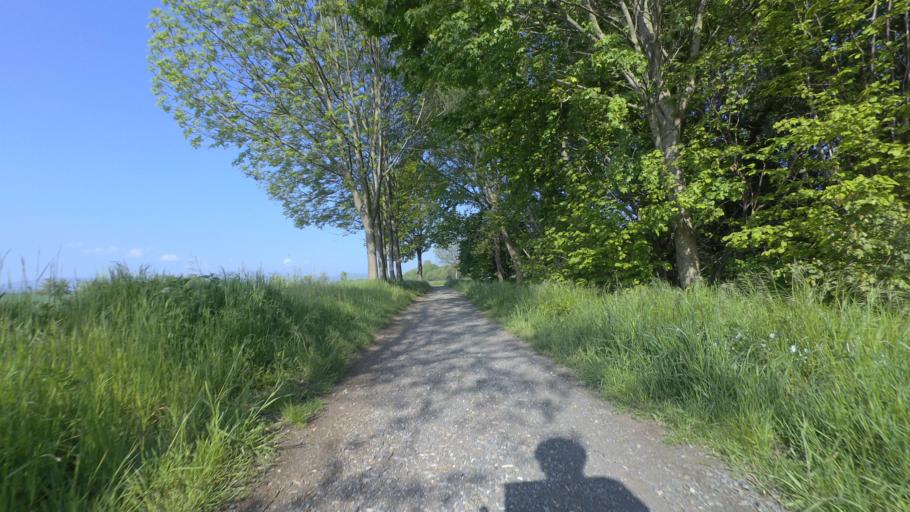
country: DE
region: Saxony-Anhalt
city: Heudeber
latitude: 51.8626
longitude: 10.8339
